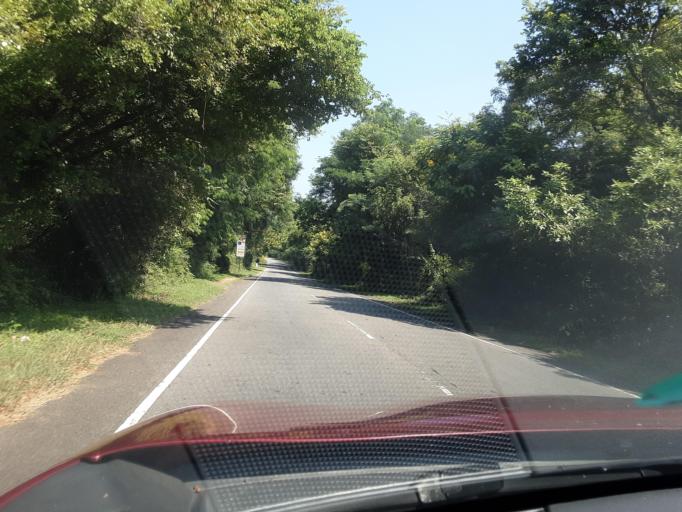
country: LK
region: Uva
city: Badulla
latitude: 7.2676
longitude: 81.0519
